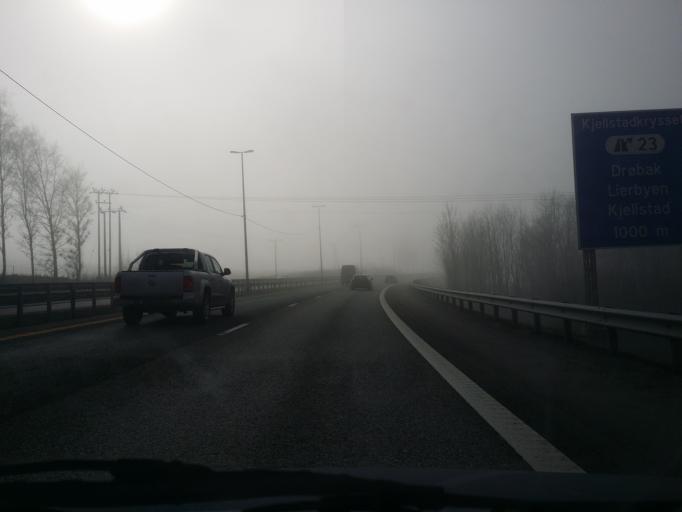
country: NO
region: Buskerud
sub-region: Lier
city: Lierbyen
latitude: 59.7794
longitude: 10.2764
